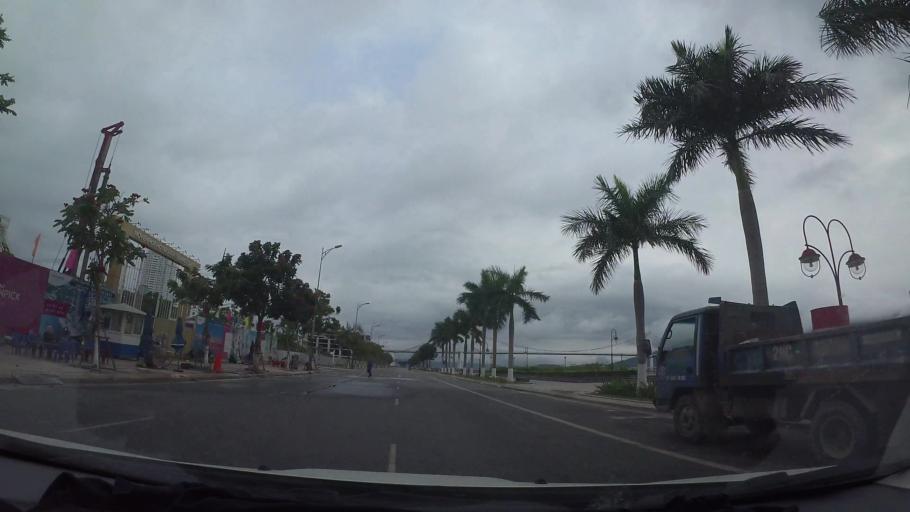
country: VN
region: Da Nang
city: Da Nang
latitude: 16.0876
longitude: 108.2211
